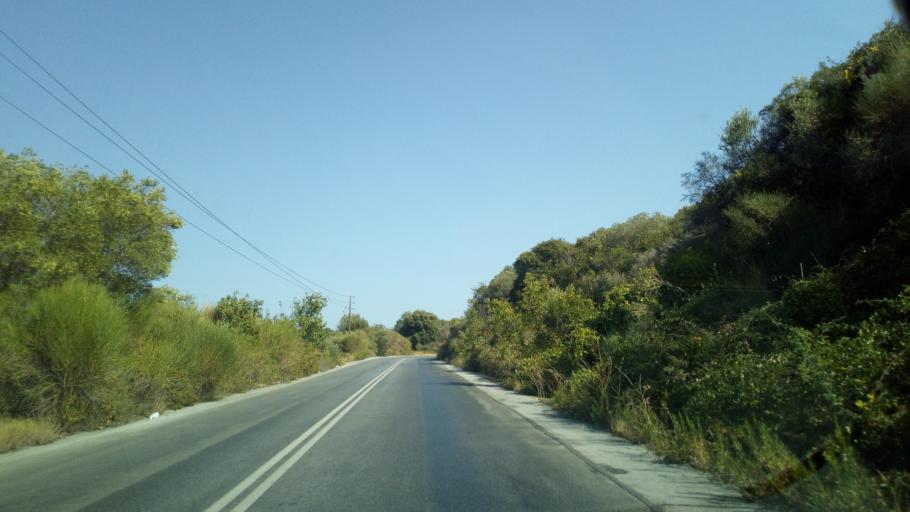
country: GR
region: Central Macedonia
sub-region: Nomos Thessalonikis
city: Stavros
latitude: 40.6226
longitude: 23.7694
